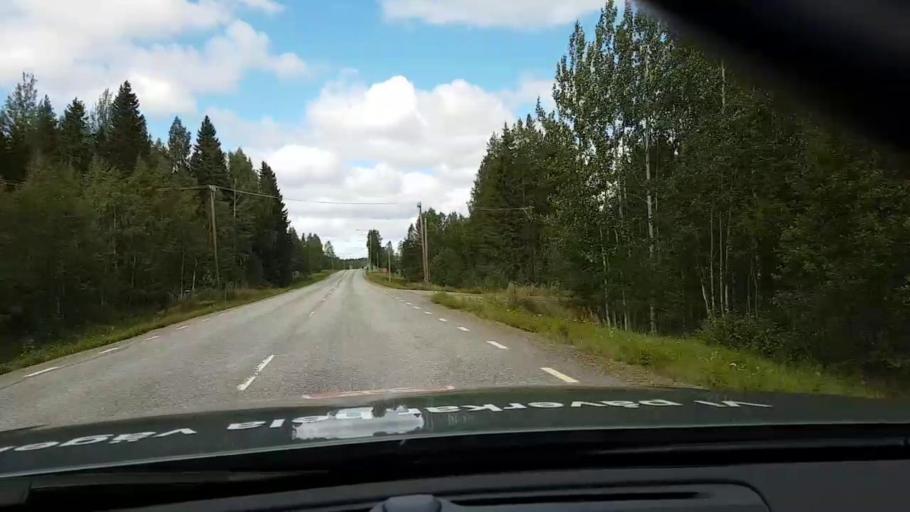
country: SE
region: Vaesternorrland
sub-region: OErnskoeldsviks Kommun
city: Bredbyn
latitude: 63.4740
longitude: 18.0968
